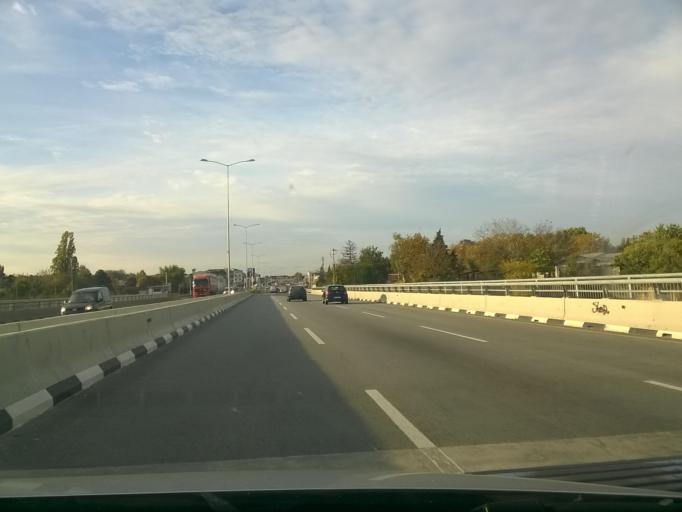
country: RS
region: Central Serbia
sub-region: Belgrade
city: Zemun
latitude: 44.8622
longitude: 20.3789
